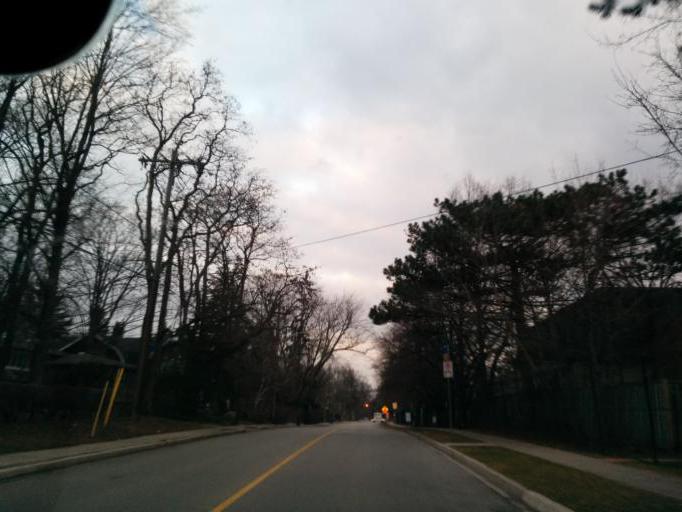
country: CA
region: Ontario
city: Oakville
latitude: 43.4540
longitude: -79.6753
